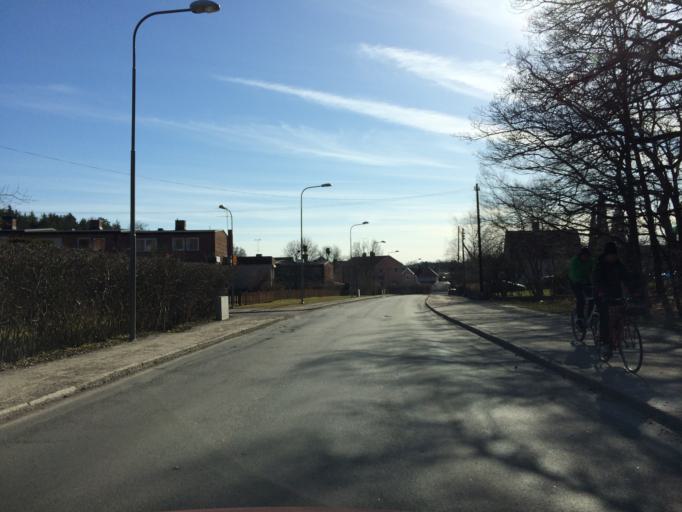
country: SE
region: Stockholm
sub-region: Huddinge Kommun
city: Huddinge
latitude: 59.2871
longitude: 17.9944
